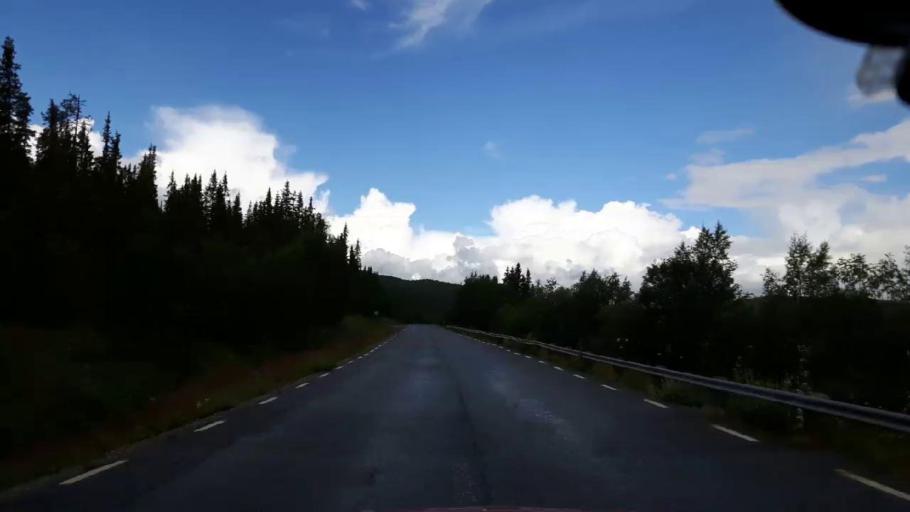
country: SE
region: Vaesterbotten
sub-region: Vilhelmina Kommun
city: Sjoberg
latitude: 65.0079
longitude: 15.1844
